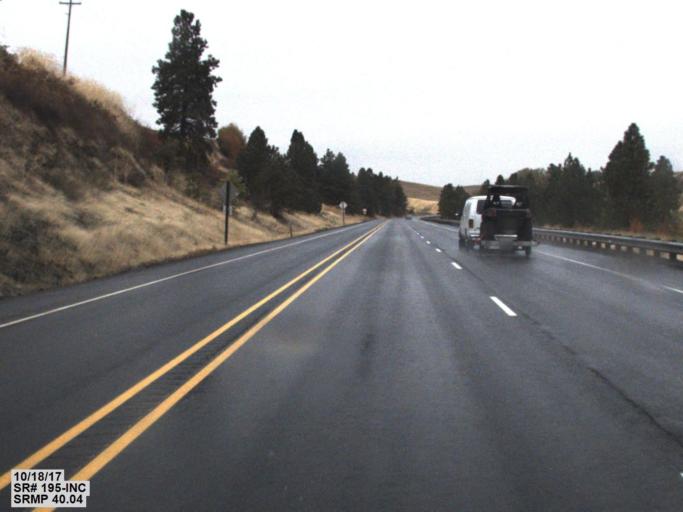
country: US
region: Washington
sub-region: Whitman County
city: Colfax
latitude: 46.9068
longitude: -117.3488
